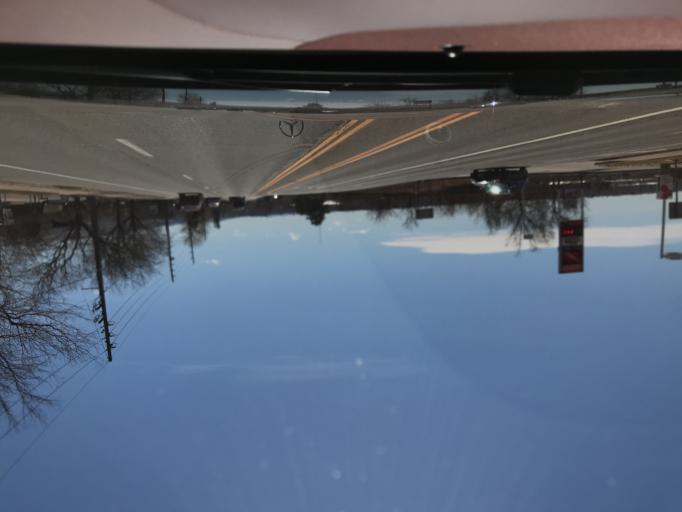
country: US
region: Colorado
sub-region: Jefferson County
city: Applewood
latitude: 39.7910
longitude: -105.1380
